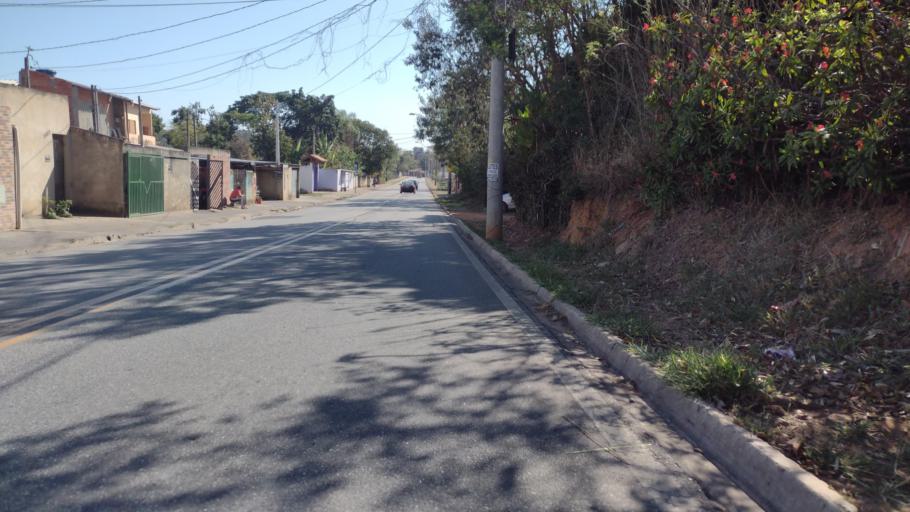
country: BR
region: Sao Paulo
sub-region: Sorocaba
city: Sorocaba
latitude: -23.4146
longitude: -47.4792
